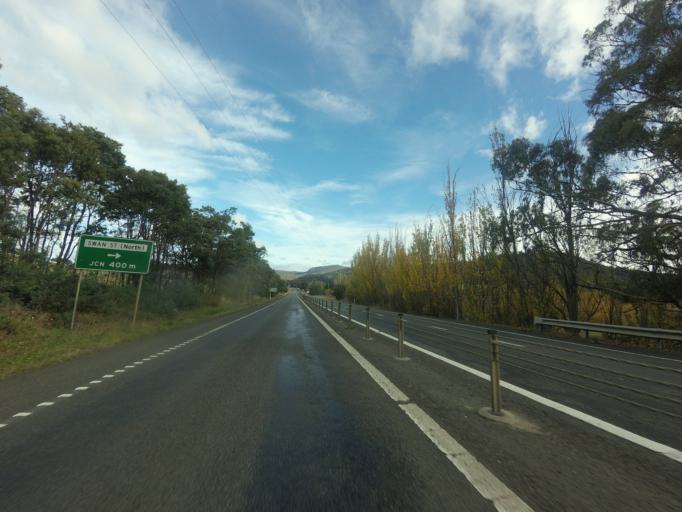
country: AU
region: Tasmania
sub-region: Brighton
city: Bridgewater
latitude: -42.5899
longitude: 147.2237
